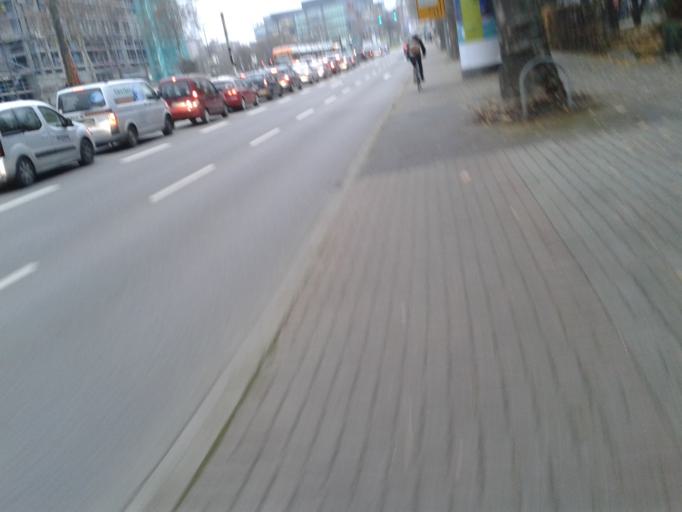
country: DE
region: Baden-Wuerttemberg
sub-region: Karlsruhe Region
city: Heidelberg
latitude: 49.4178
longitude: 8.6766
